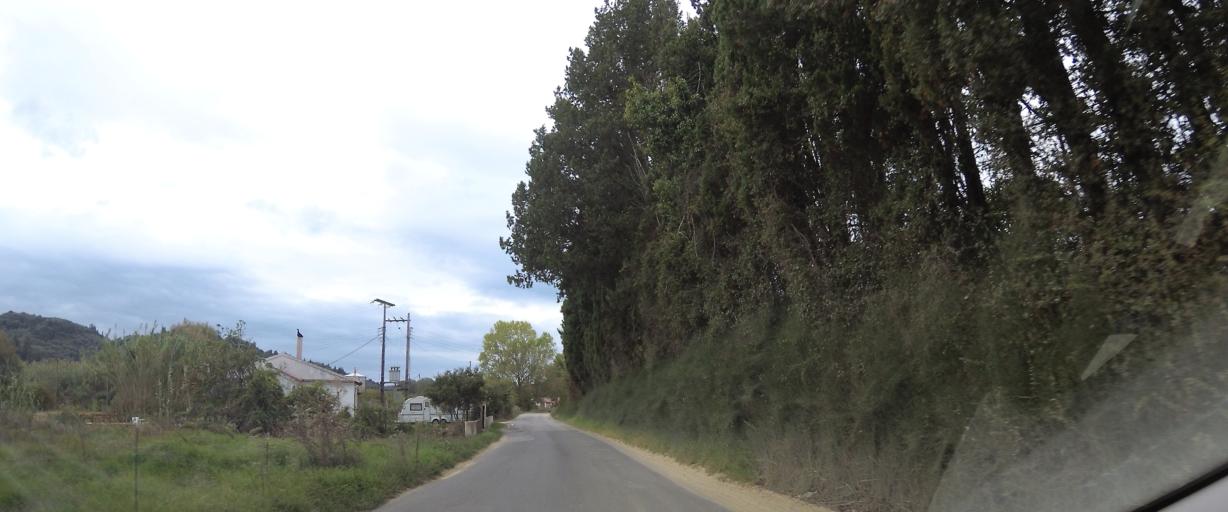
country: GR
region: Ionian Islands
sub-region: Nomos Kerkyras
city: Agios Georgis
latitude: 39.7670
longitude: 19.6972
